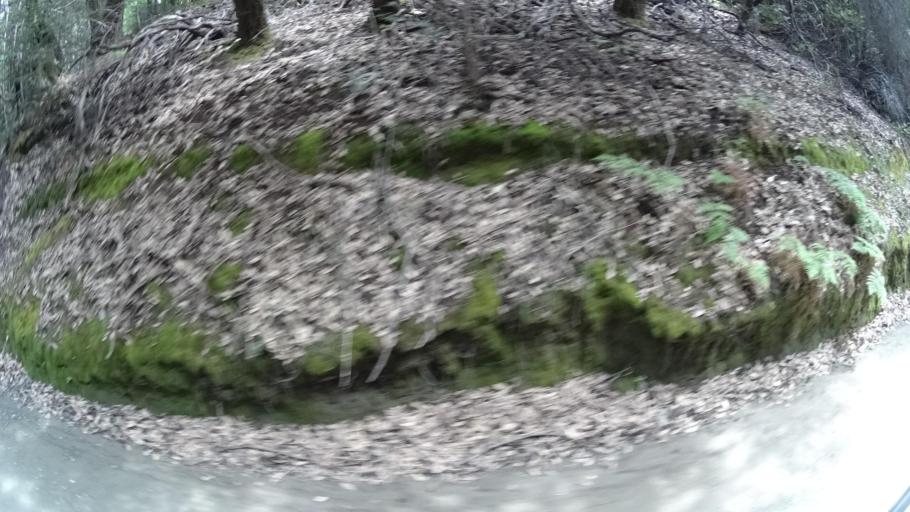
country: US
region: California
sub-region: Humboldt County
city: Redway
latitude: 40.0314
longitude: -123.8358
